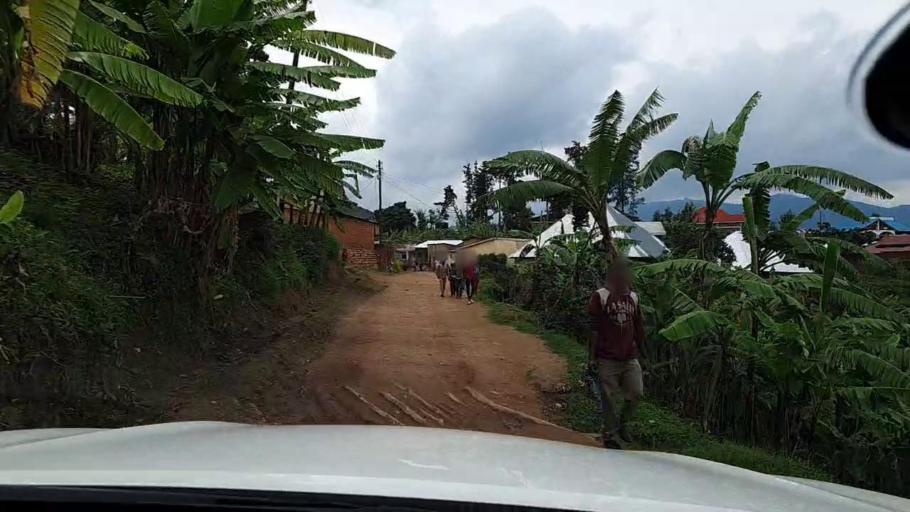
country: RW
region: Western Province
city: Kibuye
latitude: -2.1862
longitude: 29.2937
